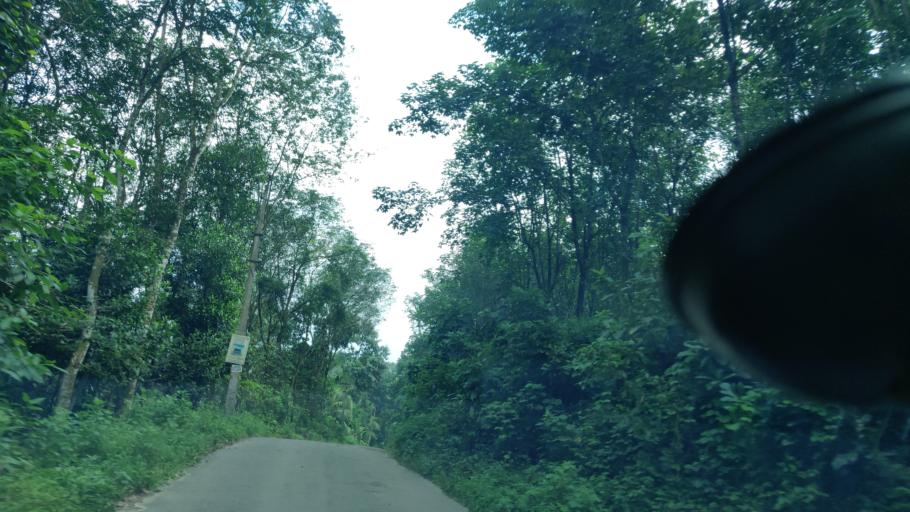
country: IN
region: Kerala
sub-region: Kottayam
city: Palackattumala
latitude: 9.8457
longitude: 76.7038
